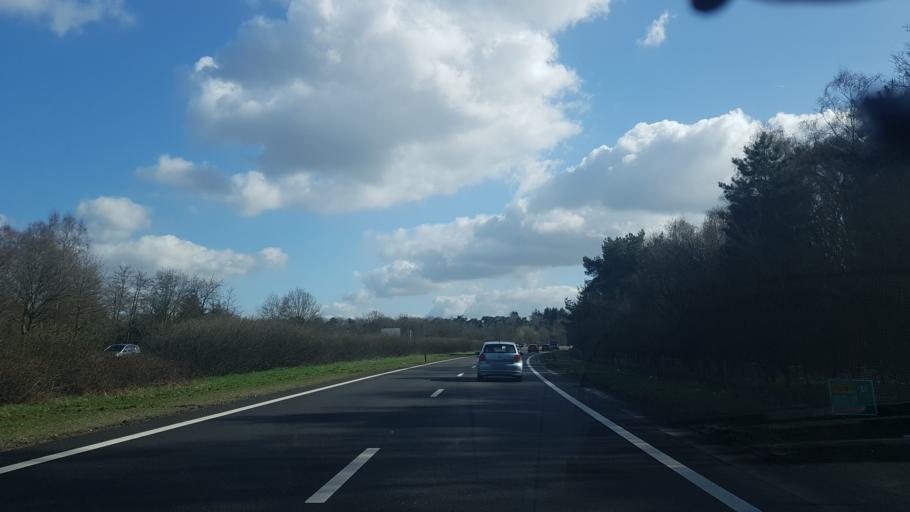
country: NL
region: North Brabant
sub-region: Gemeente Tilburg
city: Tilburg
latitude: 51.5394
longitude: 5.1158
